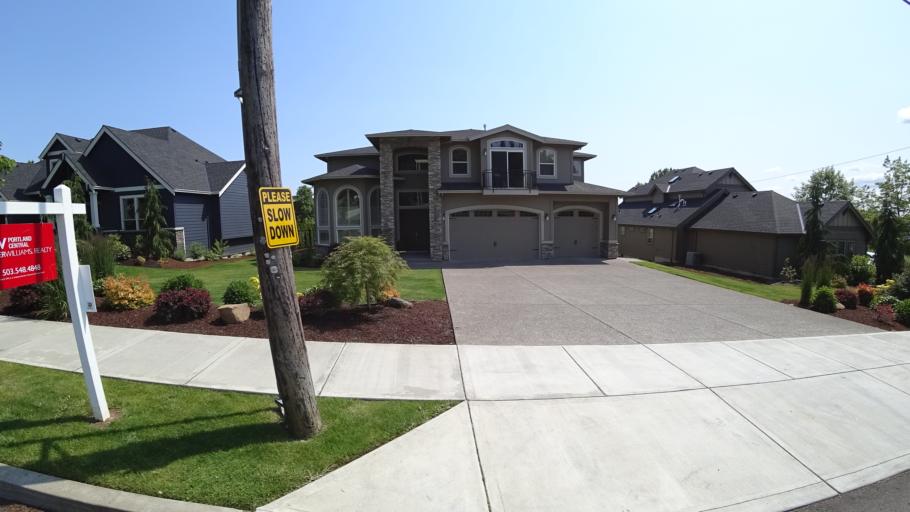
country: US
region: Oregon
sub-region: Clackamas County
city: Happy Valley
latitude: 45.4433
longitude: -122.5632
